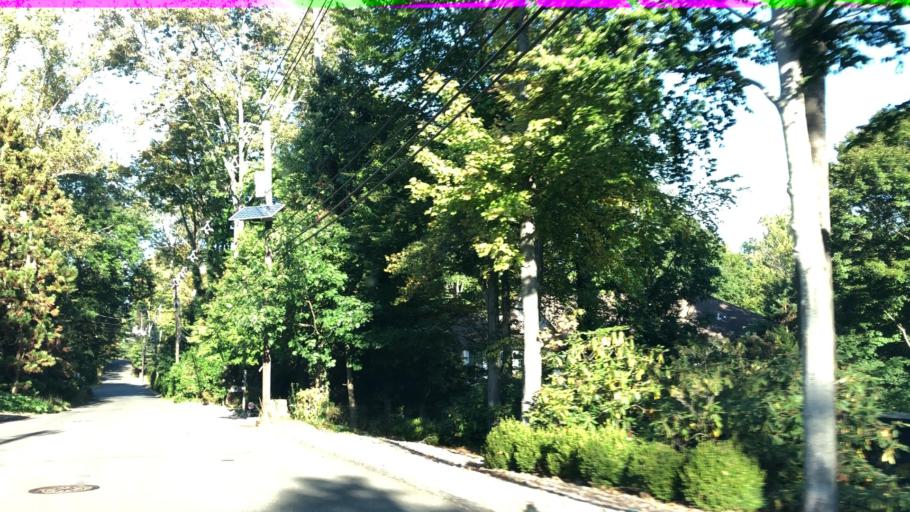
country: US
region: New Jersey
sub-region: Bergen County
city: Woodcliff Lake
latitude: 41.0318
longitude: -74.0590
